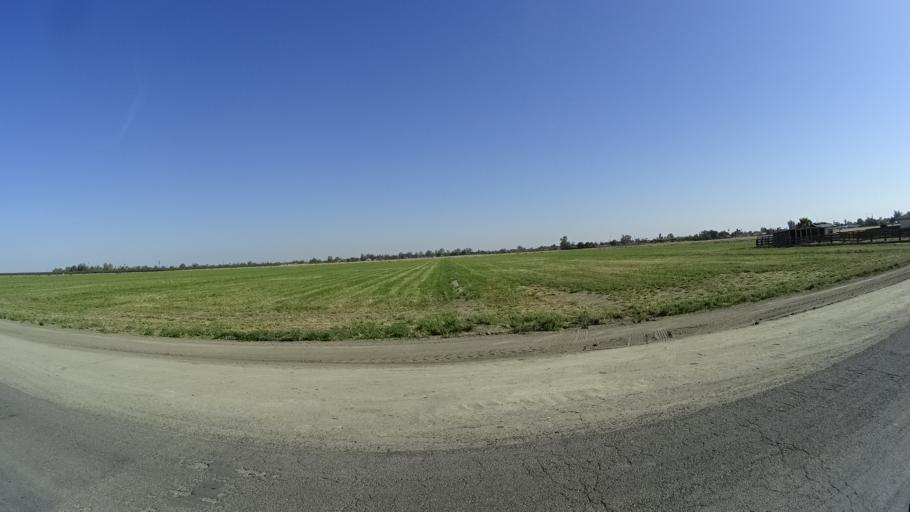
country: US
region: California
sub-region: Kings County
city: Corcoran
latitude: 36.0835
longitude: -119.5777
